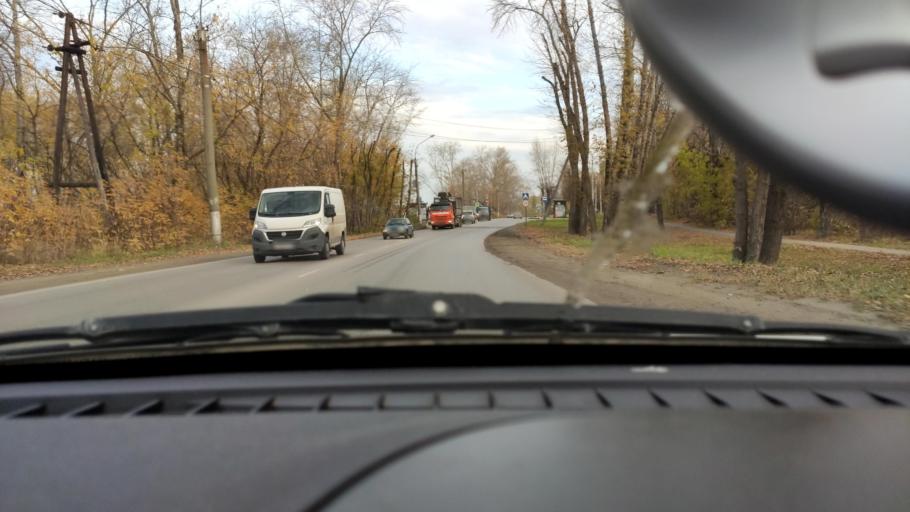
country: RU
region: Perm
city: Perm
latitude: 58.1203
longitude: 56.3690
